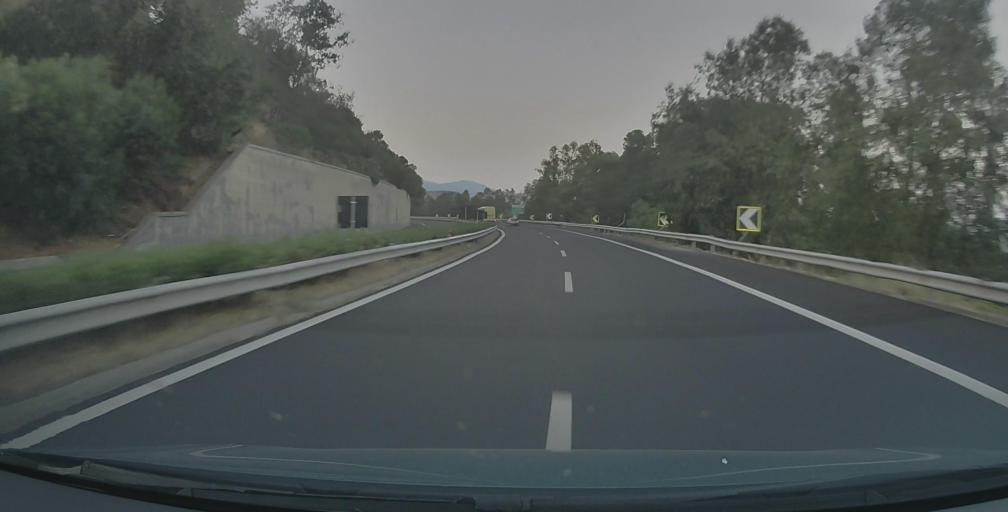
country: IT
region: Sicily
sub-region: Messina
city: Sant'Alessio Siculo
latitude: 37.9271
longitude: 15.3497
